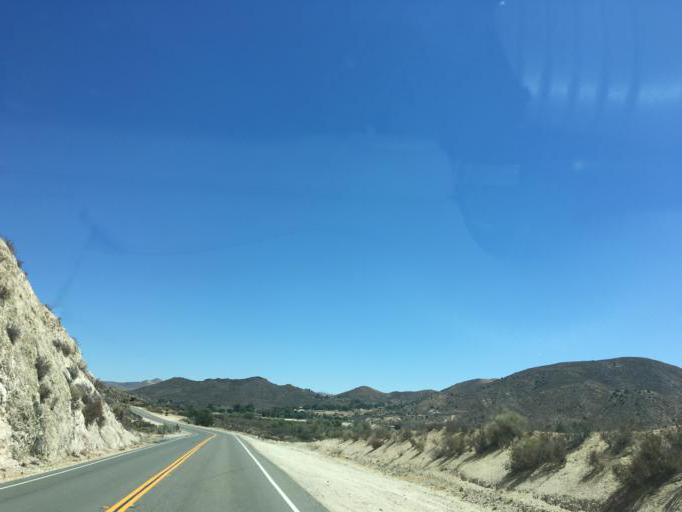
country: US
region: California
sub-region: Los Angeles County
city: Acton
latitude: 34.4494
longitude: -118.2059
